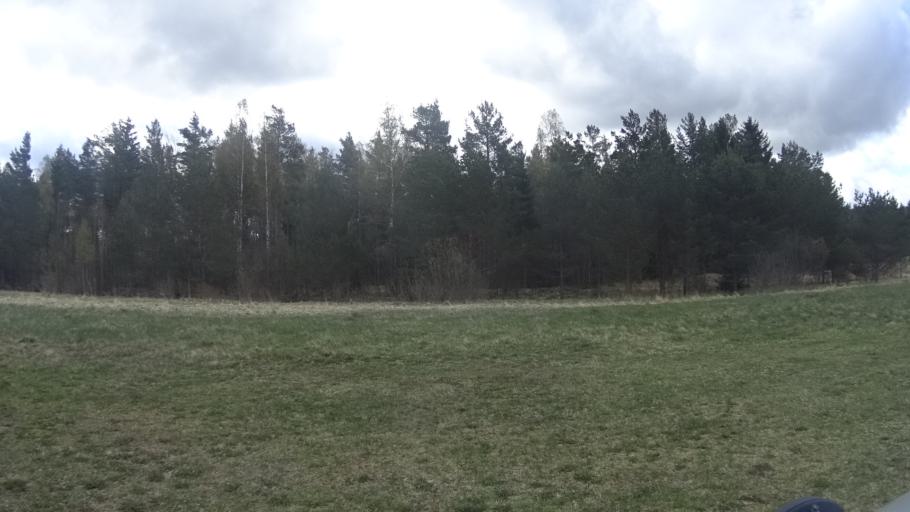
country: SE
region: Stockholm
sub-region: Botkyrka Kommun
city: Tullinge
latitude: 59.1750
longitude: 17.8915
